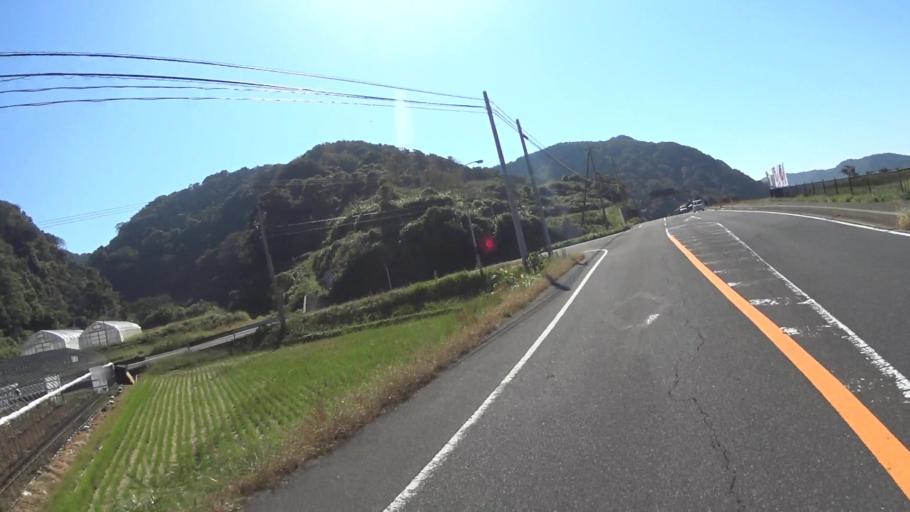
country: JP
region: Kyoto
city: Miyazu
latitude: 35.7439
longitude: 135.1205
